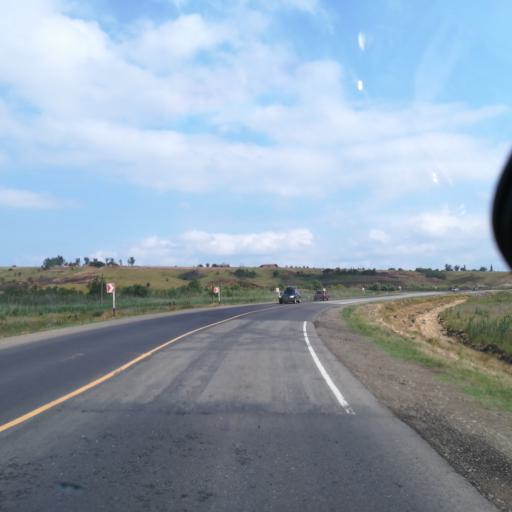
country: RU
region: Krasnodarskiy
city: Varenikovskaya
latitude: 45.1759
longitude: 37.6526
